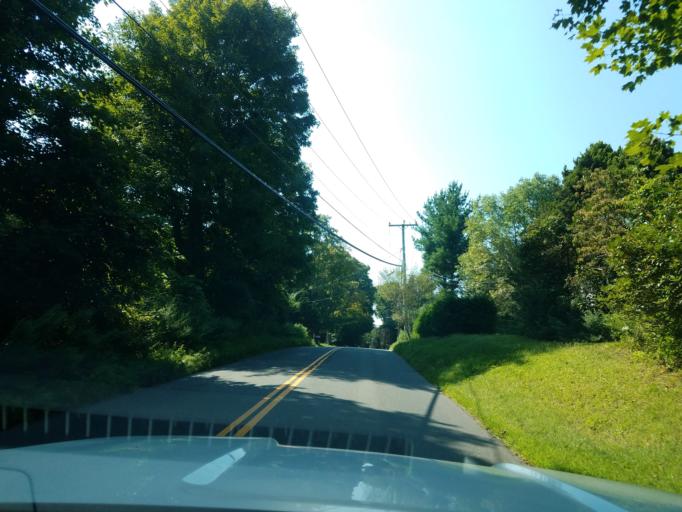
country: US
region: Connecticut
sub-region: Fairfield County
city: Newtown
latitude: 41.3669
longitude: -73.3369
